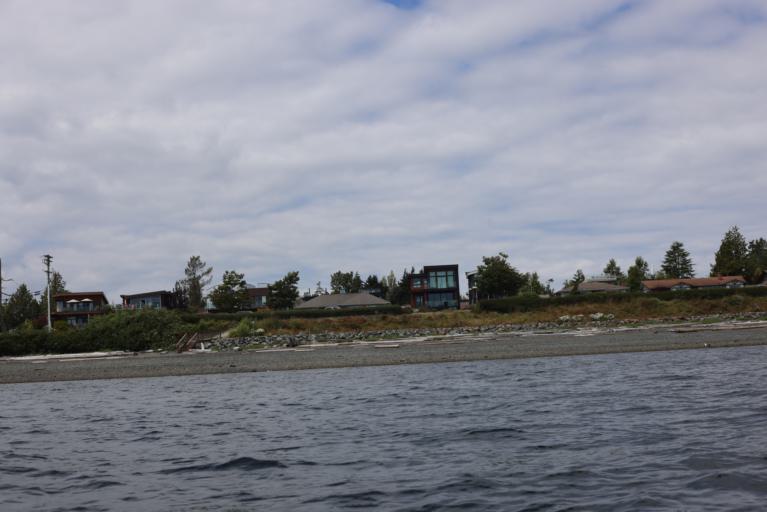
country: CA
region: British Columbia
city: North Saanich
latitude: 48.6351
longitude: -123.4034
